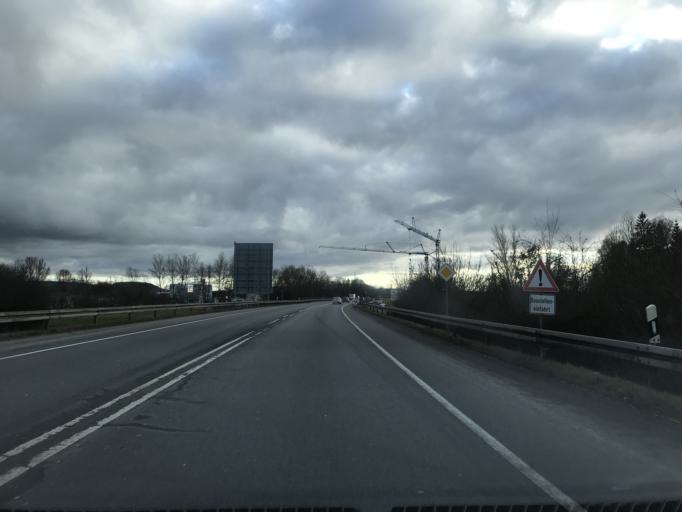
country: DE
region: Baden-Wuerttemberg
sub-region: Freiburg Region
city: Donaueschingen
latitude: 47.9531
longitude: 8.5213
